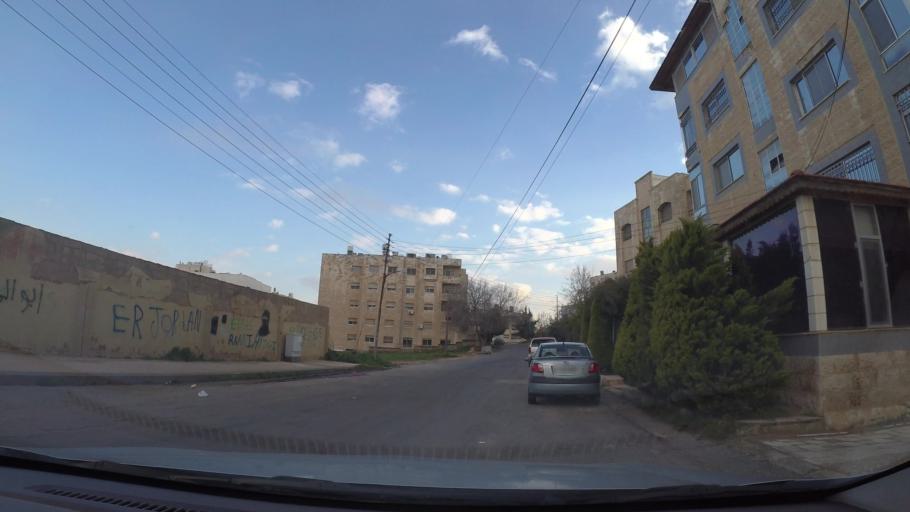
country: JO
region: Amman
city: Al Jubayhah
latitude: 31.9851
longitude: 35.8613
